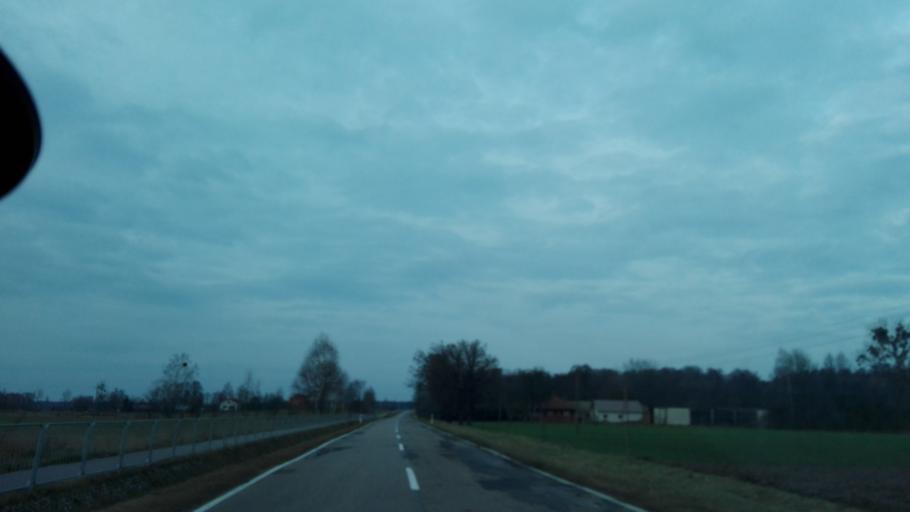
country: PL
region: Lublin Voivodeship
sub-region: Powiat bialski
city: Slawatycze
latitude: 51.6900
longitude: 23.5023
